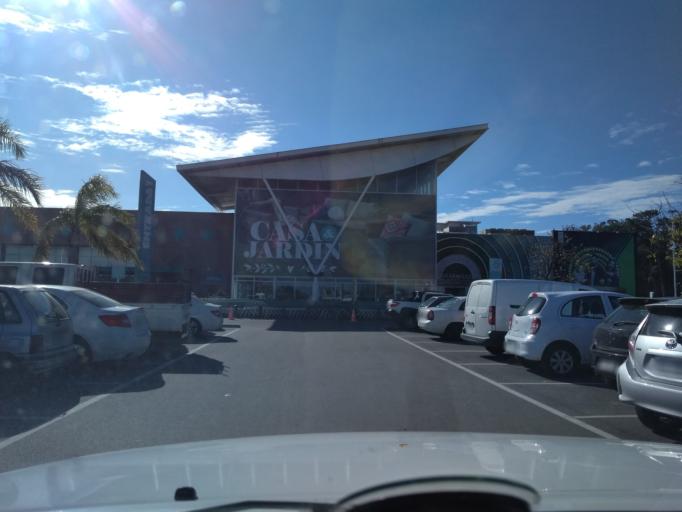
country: UY
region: Canelones
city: Barra de Carrasco
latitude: -34.8659
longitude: -56.0232
